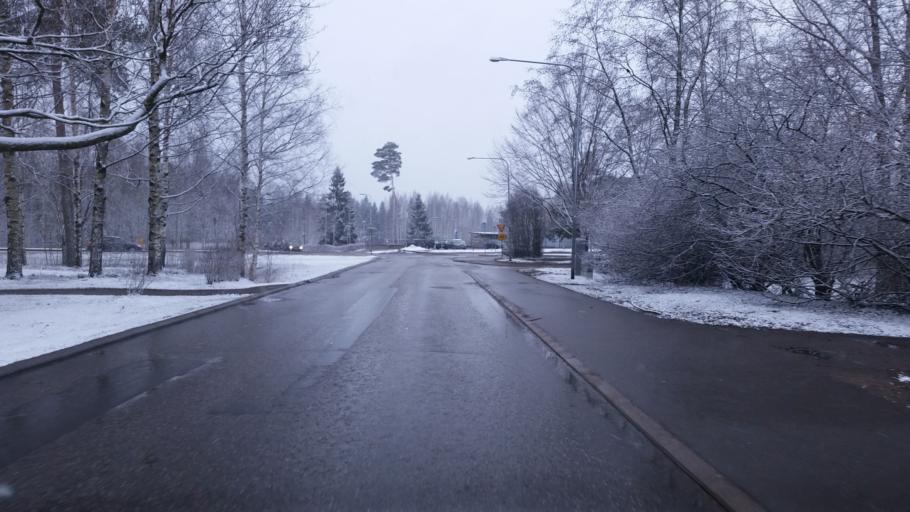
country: FI
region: Uusimaa
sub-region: Helsinki
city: Koukkuniemi
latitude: 60.1632
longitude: 24.7784
